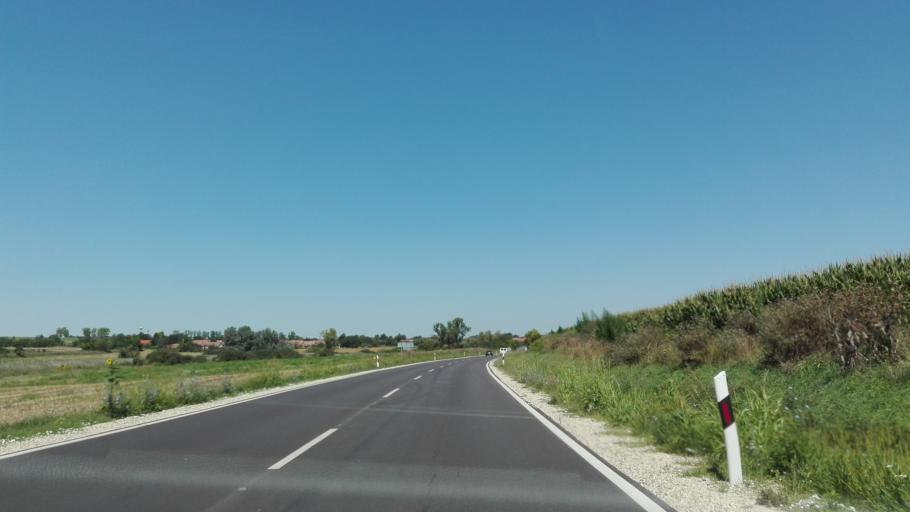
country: HU
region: Tolna
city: Simontornya
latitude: 46.7641
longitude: 18.5238
